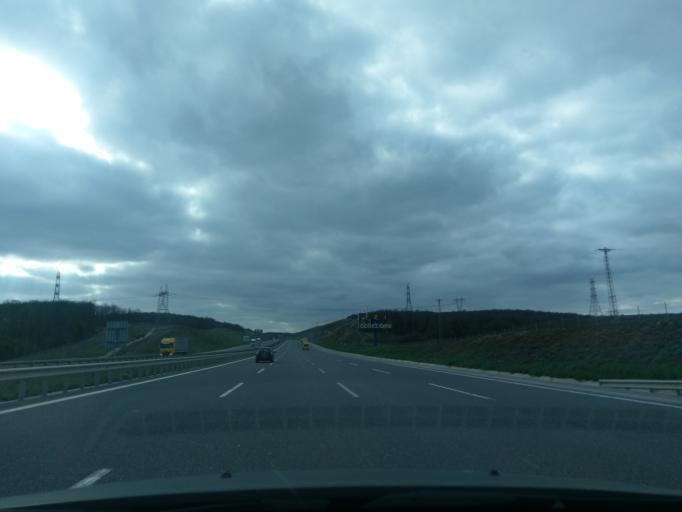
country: TR
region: Istanbul
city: Basaksehir
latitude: 41.1830
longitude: 28.8180
